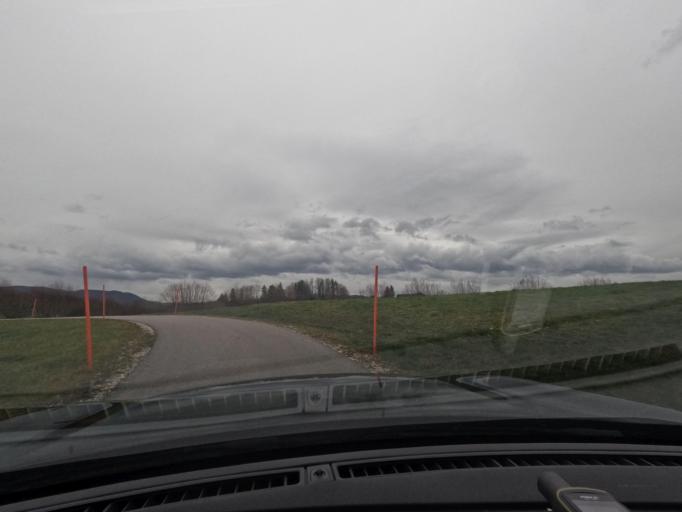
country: DE
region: Bavaria
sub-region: Upper Bavaria
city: Surberg
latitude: 47.8655
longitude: 12.6911
